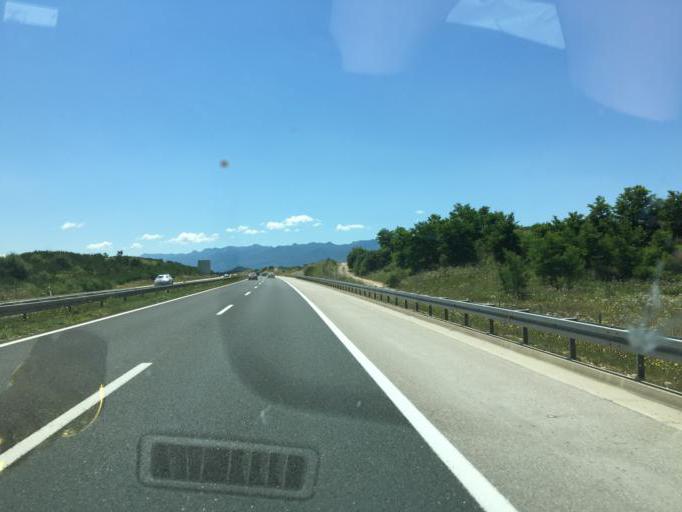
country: HR
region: Licko-Senjska
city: Gospic
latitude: 44.5628
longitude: 15.4273
